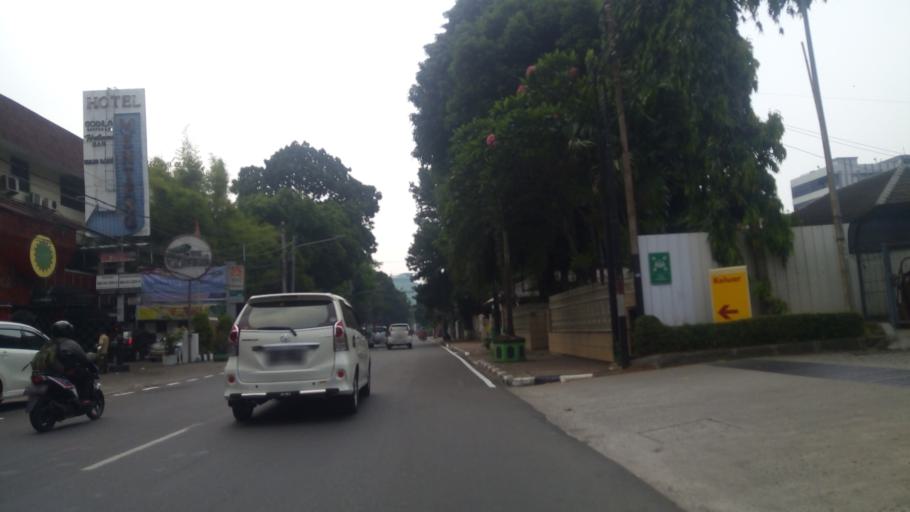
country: ID
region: Jakarta Raya
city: Jakarta
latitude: -6.1911
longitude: 106.8364
